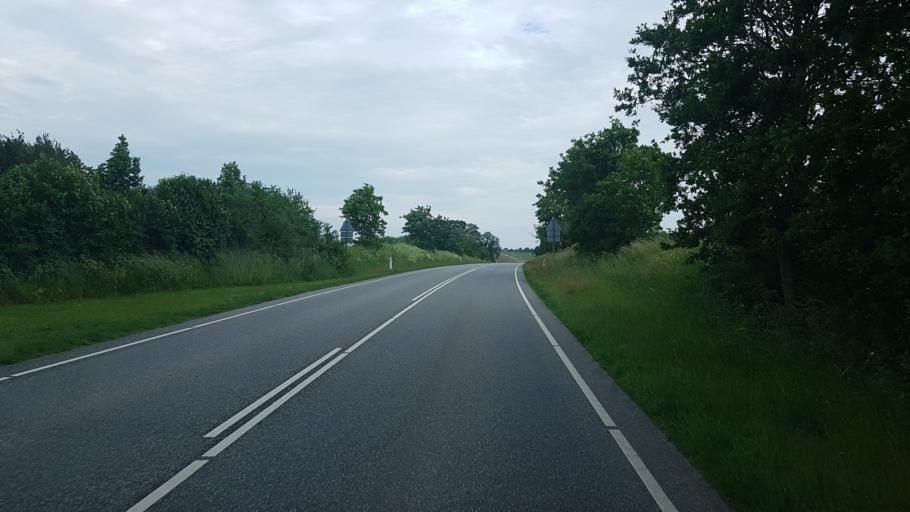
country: DK
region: South Denmark
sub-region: Vejen Kommune
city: Rodding
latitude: 55.3917
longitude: 9.0415
